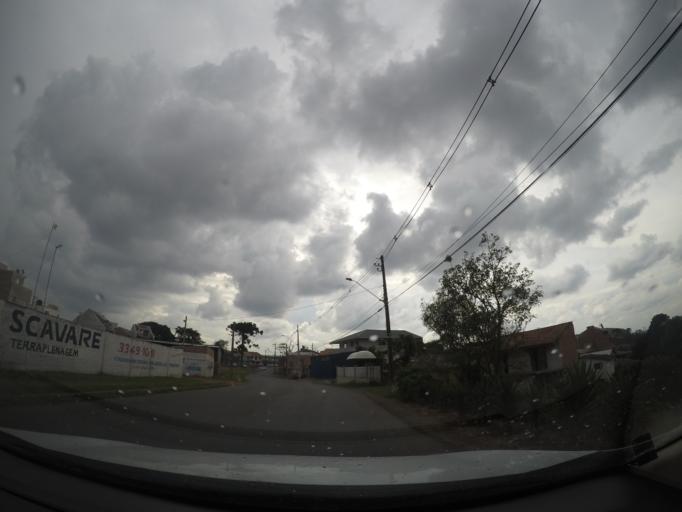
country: BR
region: Parana
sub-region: Sao Jose Dos Pinhais
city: Sao Jose dos Pinhais
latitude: -25.5446
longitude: -49.2413
